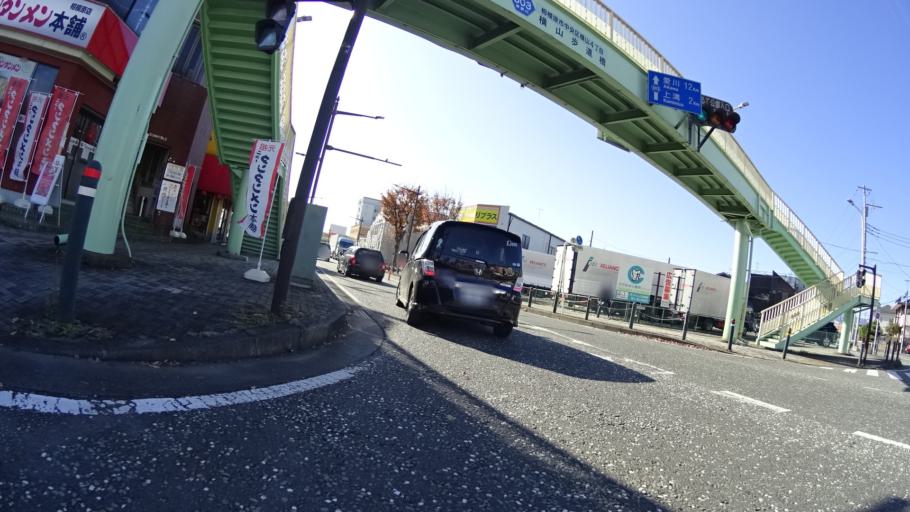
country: JP
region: Kanagawa
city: Zama
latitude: 35.5681
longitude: 139.3610
